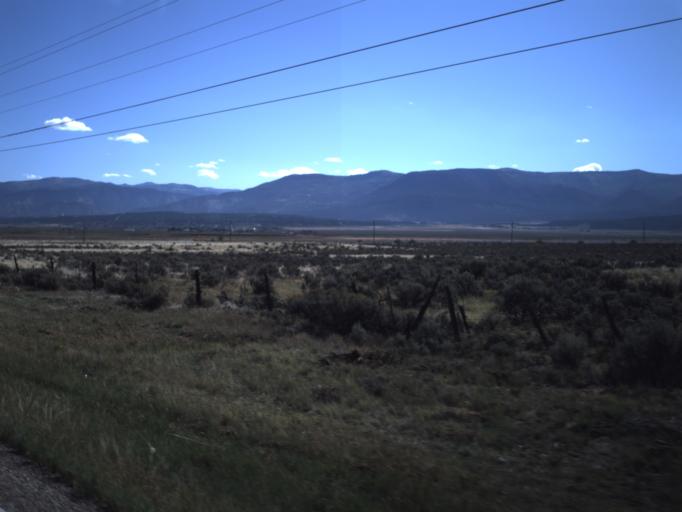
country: US
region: Utah
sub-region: Iron County
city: Cedar City
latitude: 37.6518
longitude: -113.2307
